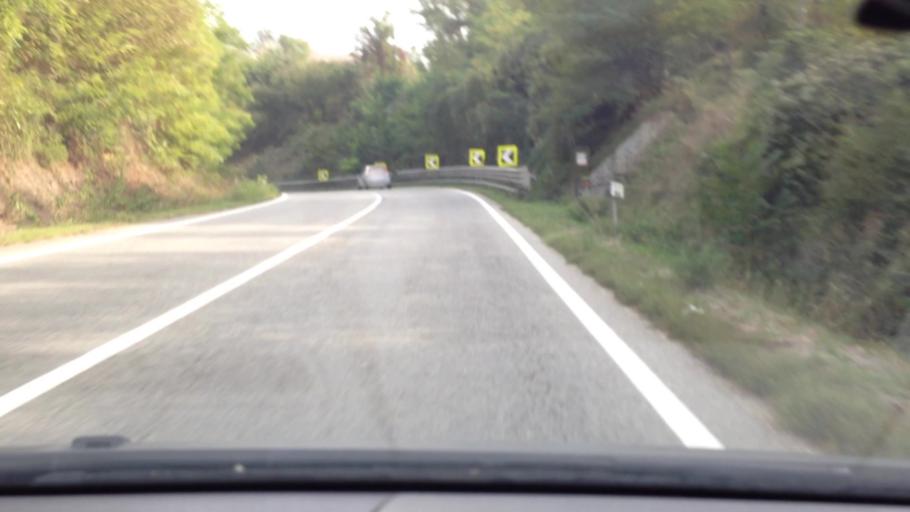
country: IT
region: Piedmont
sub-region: Provincia di Asti
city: Castello di Annone
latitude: 44.8904
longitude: 8.3037
